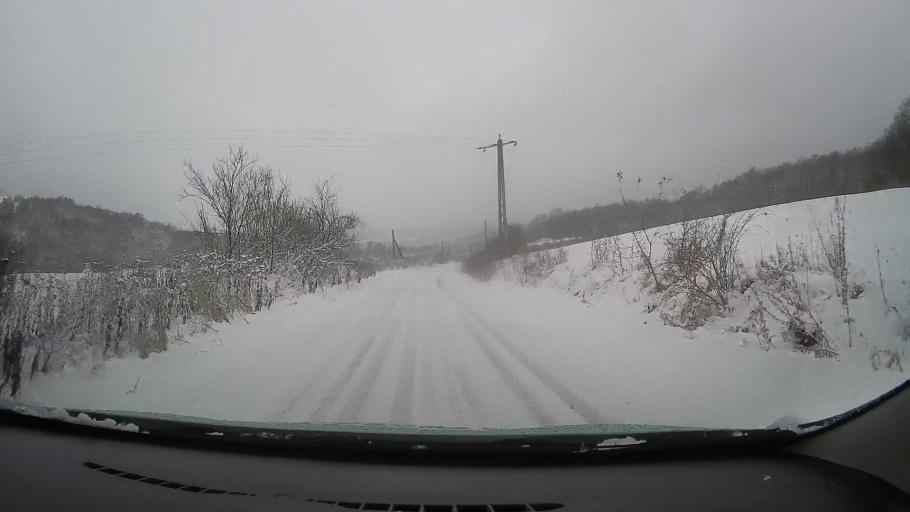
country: RO
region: Hunedoara
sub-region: Comuna Carjiti
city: Carjiti
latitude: 45.8378
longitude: 22.8372
